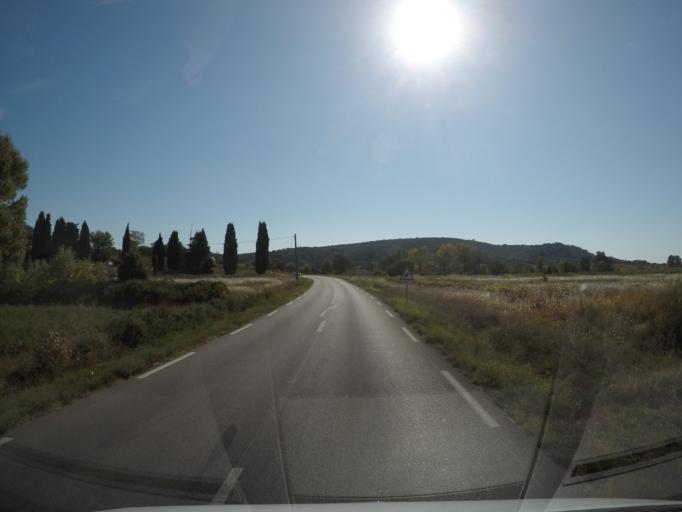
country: FR
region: Languedoc-Roussillon
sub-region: Departement du Gard
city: Ledignan
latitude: 44.0074
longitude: 4.1225
